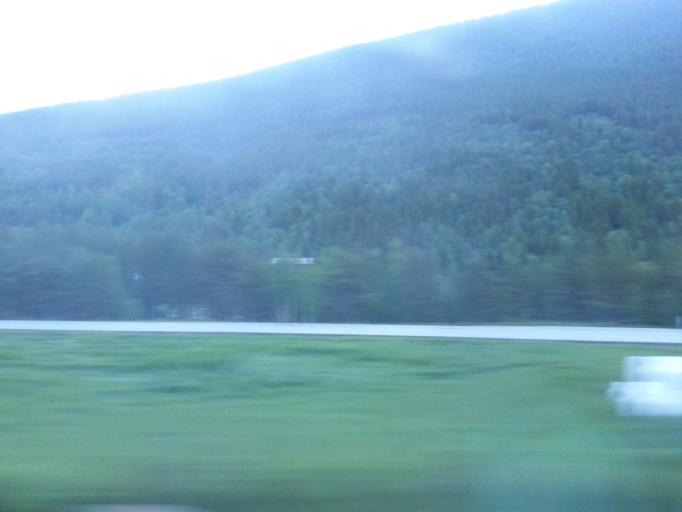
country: NO
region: Oppland
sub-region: Dovre
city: Dovre
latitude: 61.9477
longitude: 9.2946
